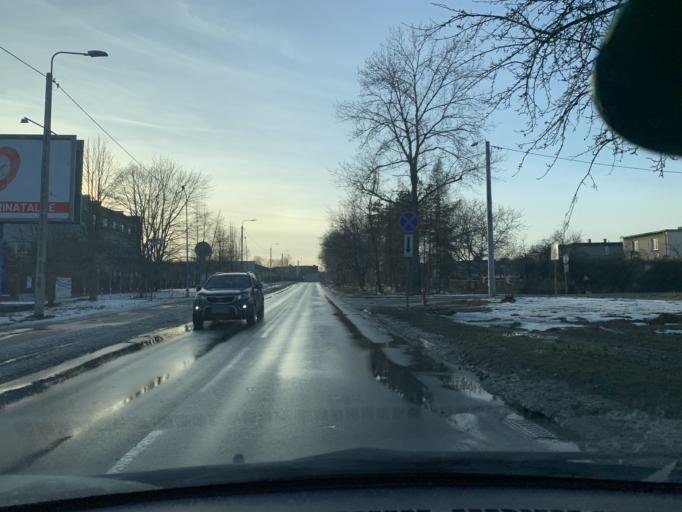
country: PL
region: Silesian Voivodeship
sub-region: Powiat tarnogorski
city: Radzionkow
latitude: 50.3850
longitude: 18.8961
